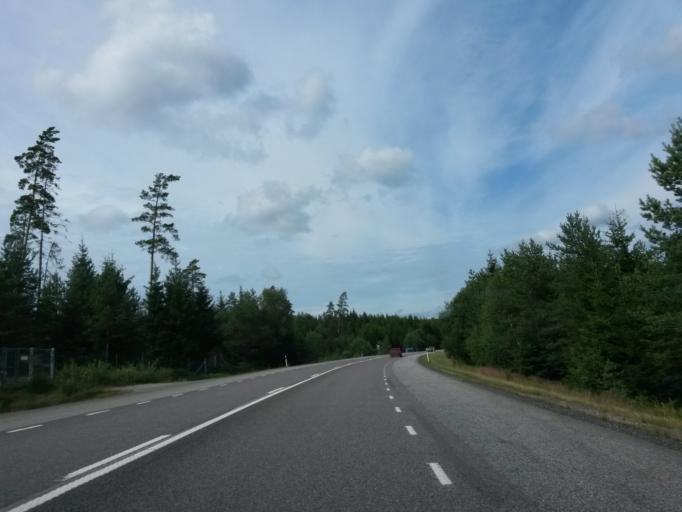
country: SE
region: Vaestra Goetaland
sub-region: Boras Kommun
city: Viskafors
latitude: 57.6097
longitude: 12.8721
